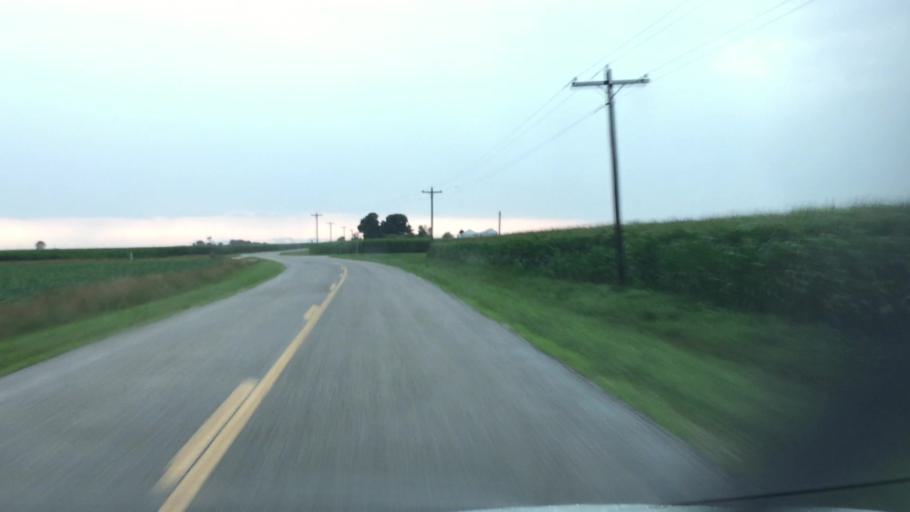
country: US
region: Iowa
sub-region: Lee County
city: Fort Madison
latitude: 40.5210
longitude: -91.2485
